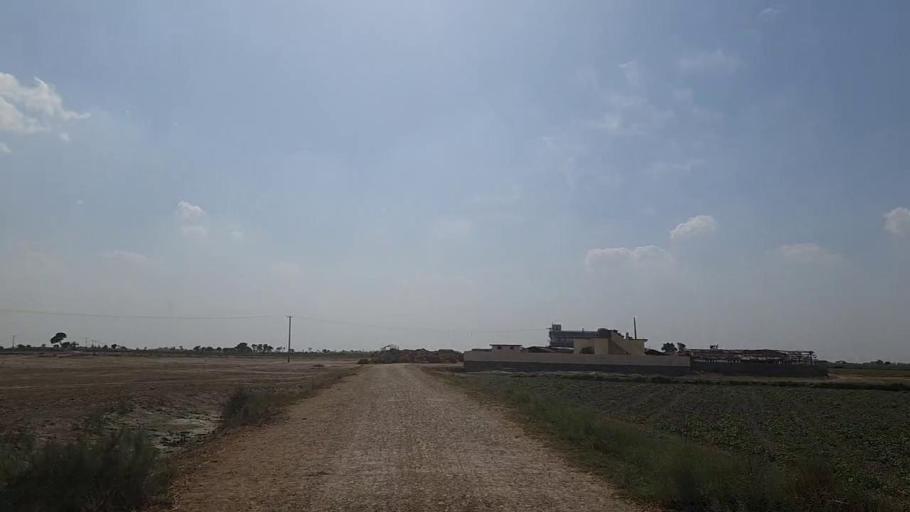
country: PK
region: Sindh
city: Jati
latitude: 24.4791
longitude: 68.2665
